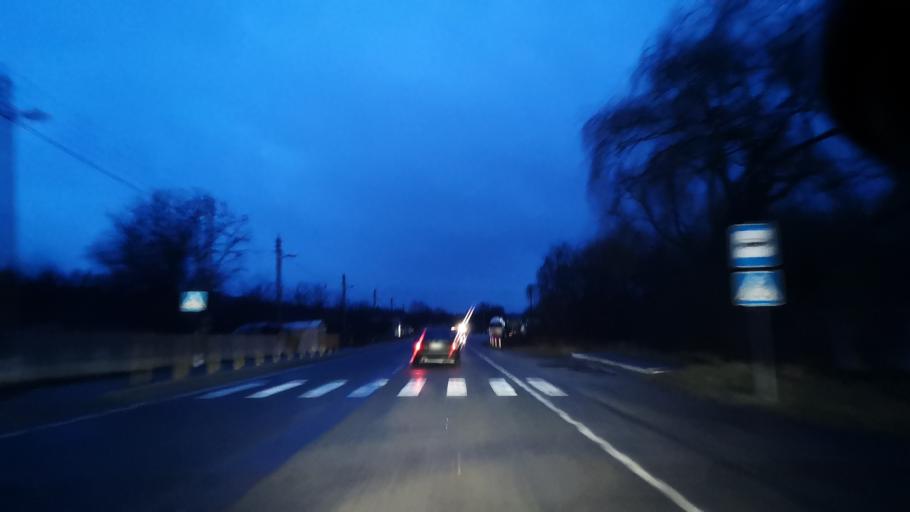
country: MD
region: Orhei
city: Orhei
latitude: 47.4283
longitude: 28.8021
